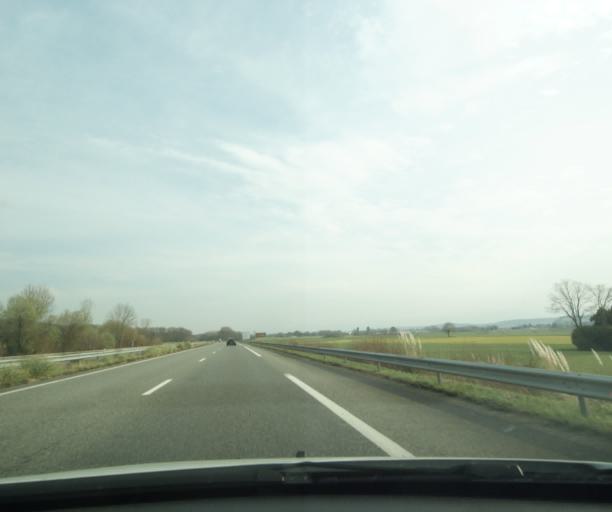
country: FR
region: Aquitaine
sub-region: Departement des Pyrenees-Atlantiques
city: Nousty
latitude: 43.2917
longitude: -0.2235
